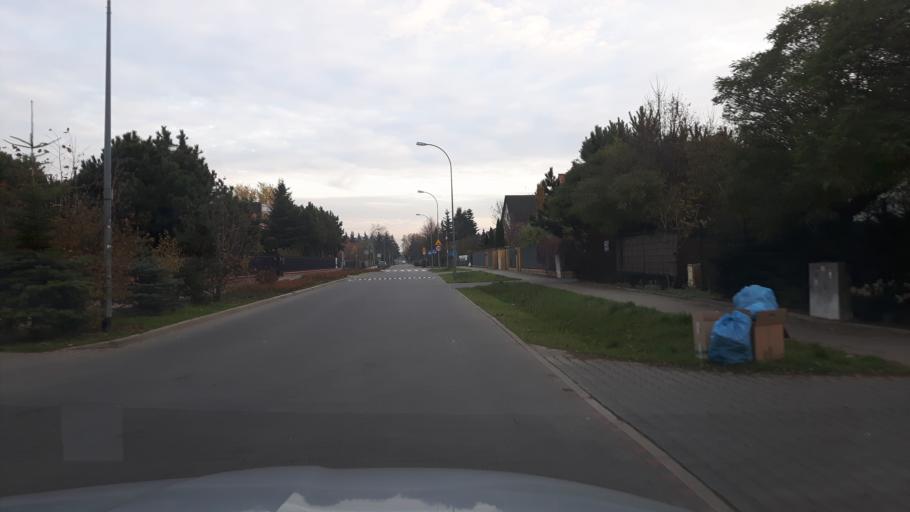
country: PL
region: Masovian Voivodeship
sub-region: Warszawa
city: Wilanow
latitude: 52.1755
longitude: 21.1103
